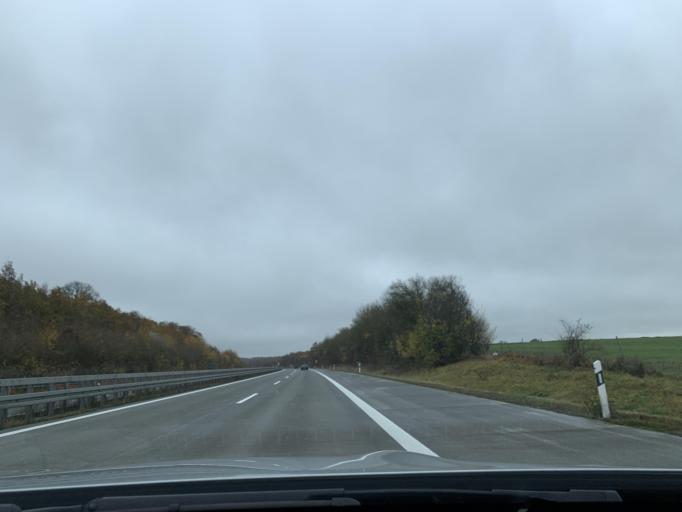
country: DE
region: Baden-Wuerttemberg
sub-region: Regierungsbezirk Stuttgart
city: Buch am Ahorn
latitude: 49.5100
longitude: 9.5656
